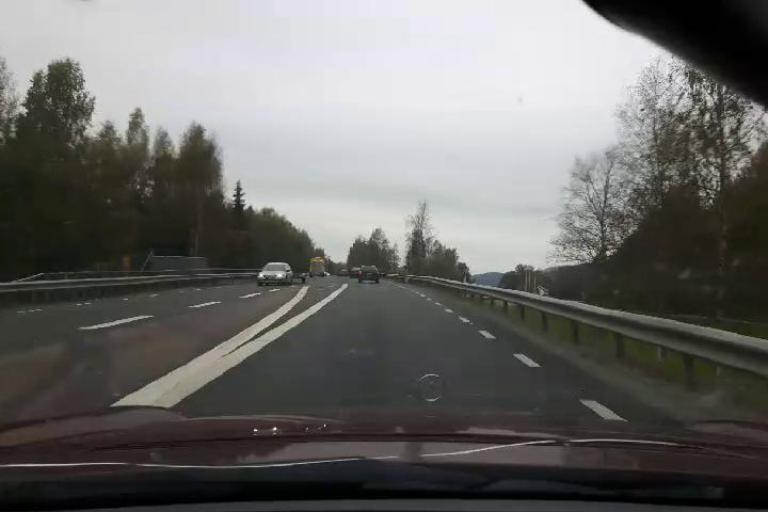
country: SE
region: Vaesternorrland
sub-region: OErnskoeldsviks Kommun
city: Ornskoldsvik
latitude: 63.2954
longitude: 18.6772
